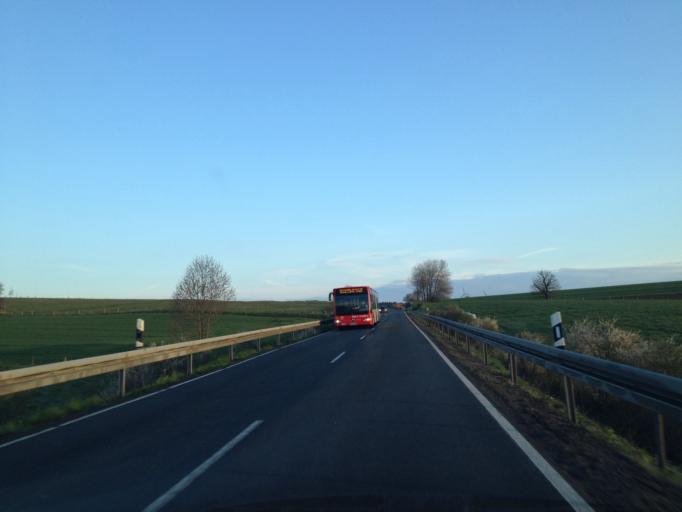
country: DE
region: North Rhine-Westphalia
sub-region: Regierungsbezirk Arnsberg
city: Mohnesee
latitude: 51.4907
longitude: 8.2164
